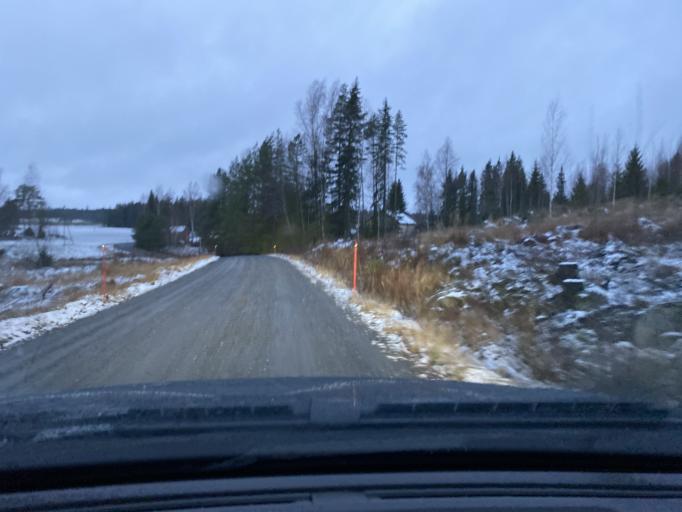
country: FI
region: Pirkanmaa
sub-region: Lounais-Pirkanmaa
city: Punkalaidun
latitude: 61.1635
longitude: 22.9586
